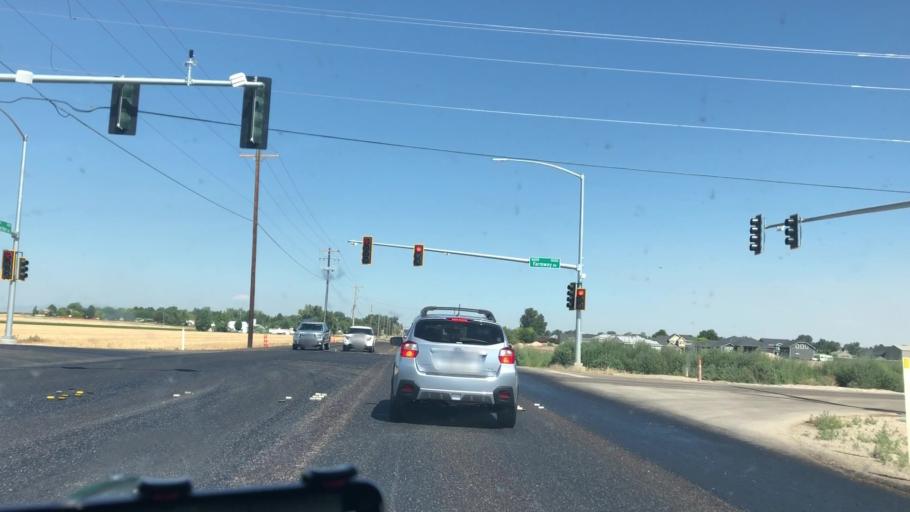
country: US
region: Idaho
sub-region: Canyon County
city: Caldwell
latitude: 43.6039
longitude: -116.7134
